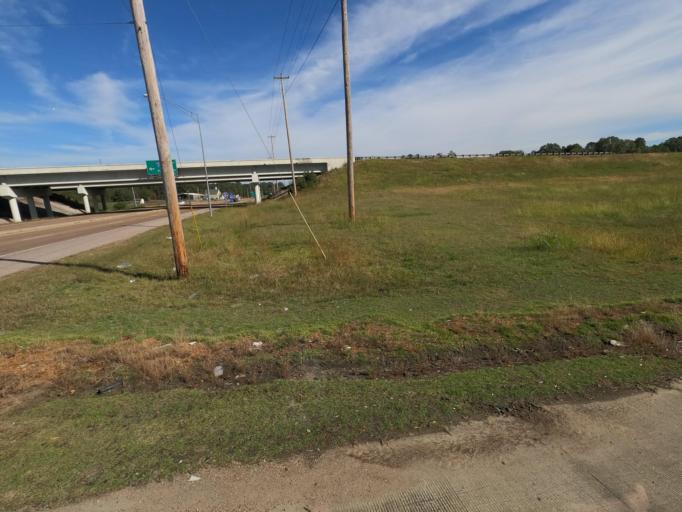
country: US
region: Tennessee
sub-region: Fayette County
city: Hickory Withe
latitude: 35.2098
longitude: -89.6551
